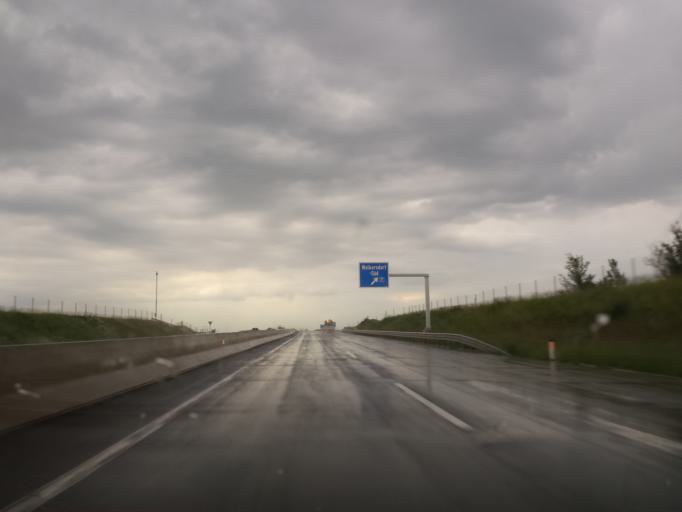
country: AT
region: Lower Austria
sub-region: Politischer Bezirk Mistelbach
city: Grossebersdorf
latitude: 48.3767
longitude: 16.4894
